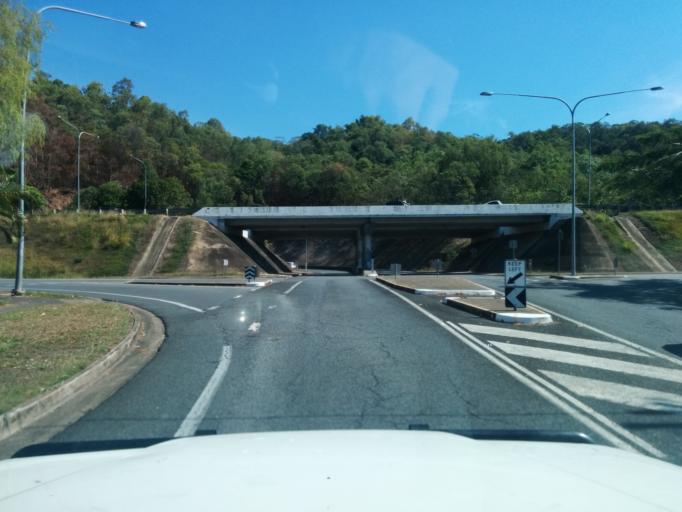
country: AU
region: Queensland
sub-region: Cairns
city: Cairns
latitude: -16.9139
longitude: 145.7279
